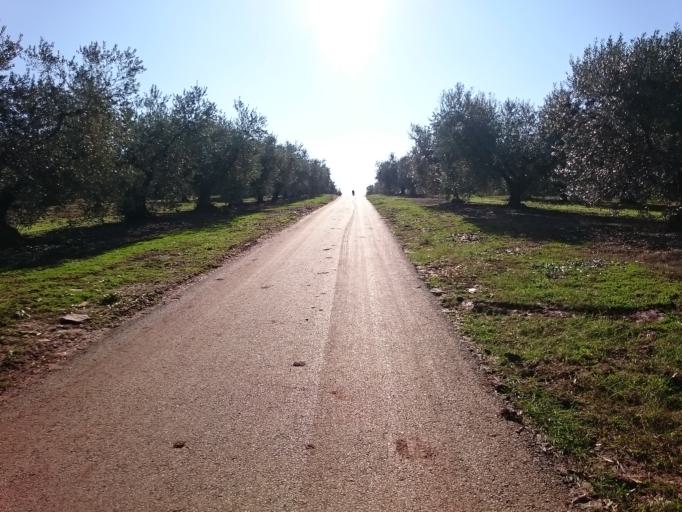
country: HR
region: Istarska
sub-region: Grad Porec
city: Porec
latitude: 45.2624
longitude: 13.5846
